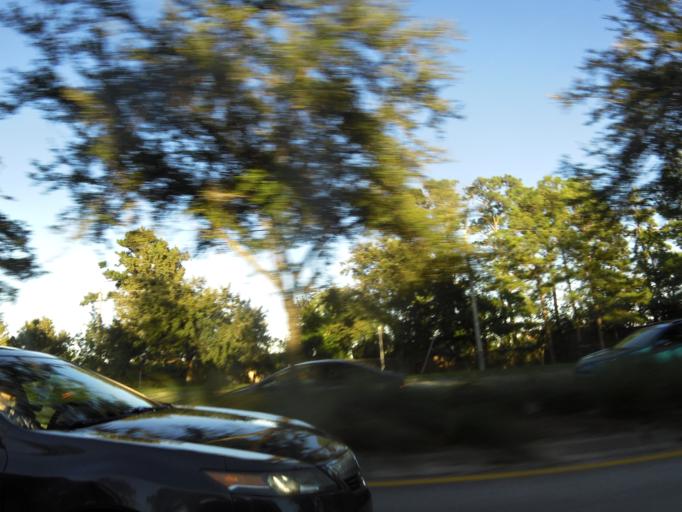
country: US
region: Florida
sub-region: Duval County
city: Jacksonville Beach
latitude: 30.2656
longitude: -81.4376
